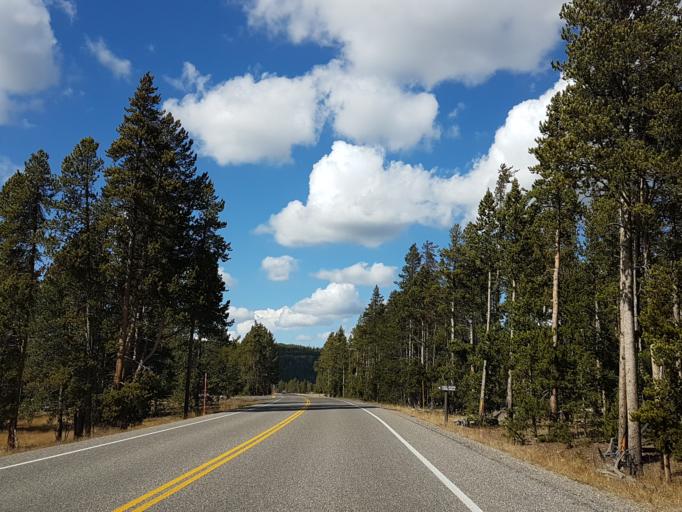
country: US
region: Montana
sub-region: Gallatin County
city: West Yellowstone
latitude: 44.5734
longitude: -110.8213
